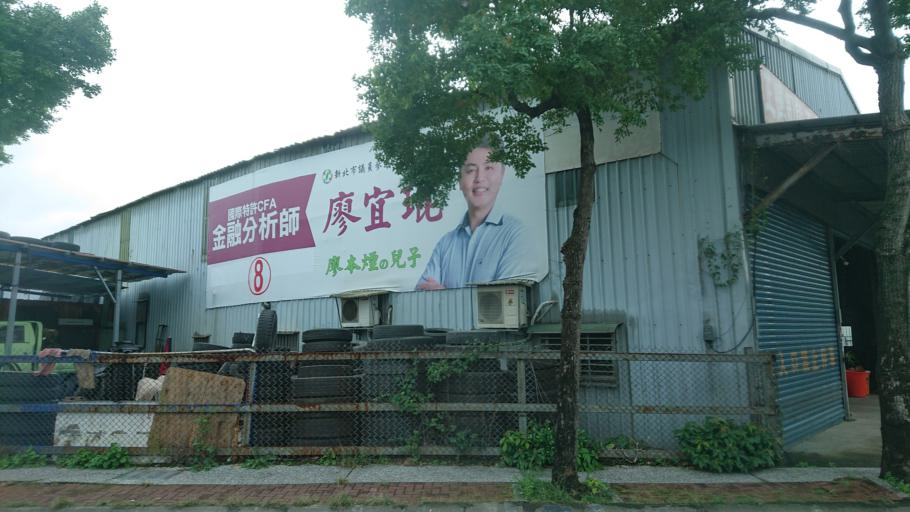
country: TW
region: Taipei
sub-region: Taipei
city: Banqiao
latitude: 24.9795
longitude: 121.4531
